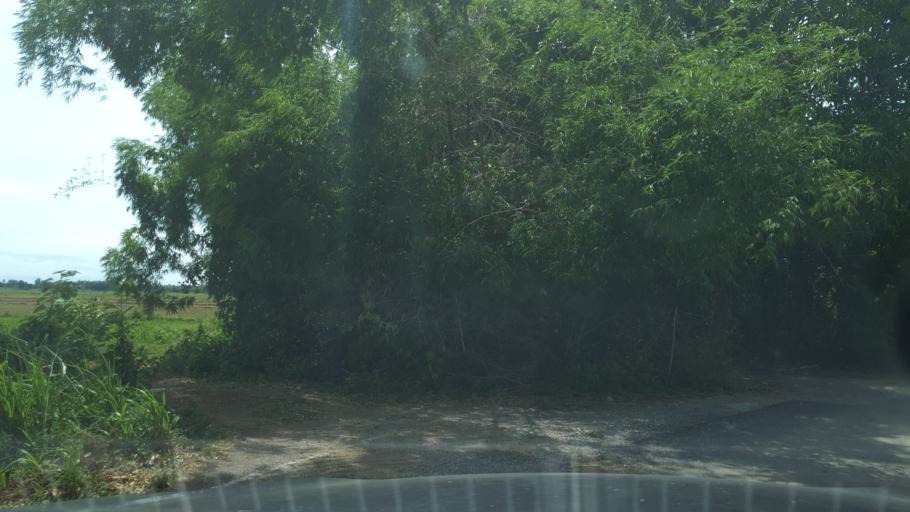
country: TH
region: Sukhothai
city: Si Samrong
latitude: 17.1992
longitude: 99.7227
